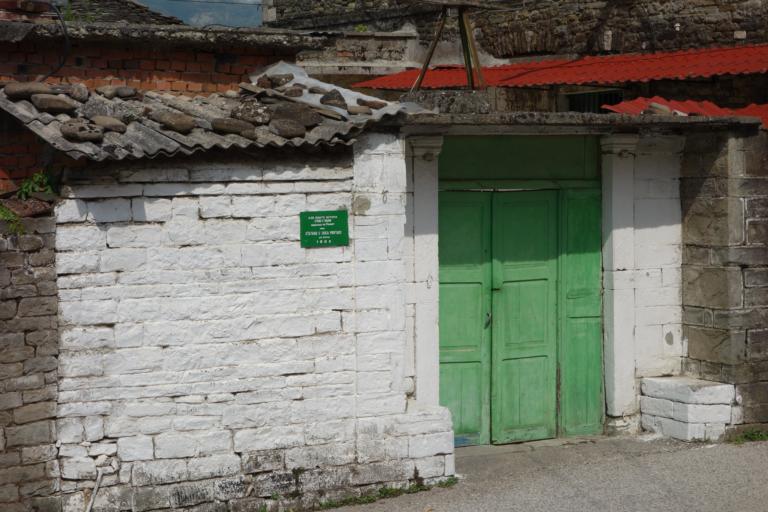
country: AL
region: Gjirokaster
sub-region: Rrethi i Permetit
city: Permet
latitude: 40.2313
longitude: 20.3531
